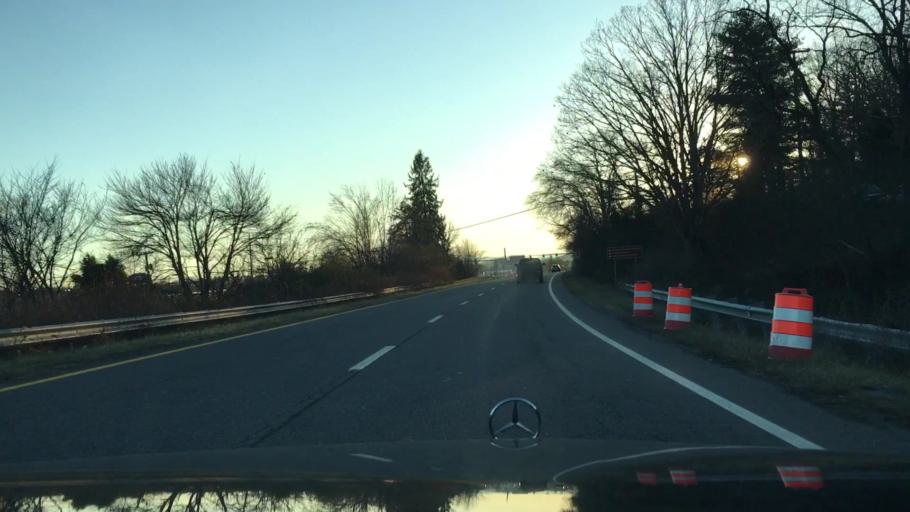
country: US
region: Virginia
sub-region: Montgomery County
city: Merrimac
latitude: 37.1814
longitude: -80.4116
